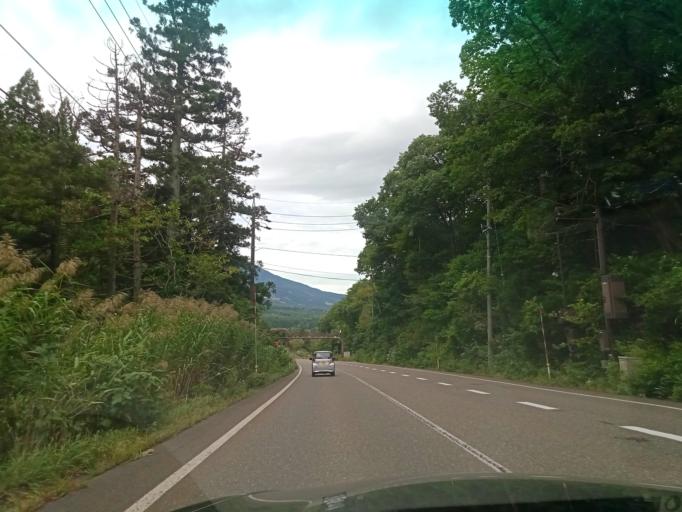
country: JP
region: Niigata
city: Arai
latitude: 36.8469
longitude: 138.1983
